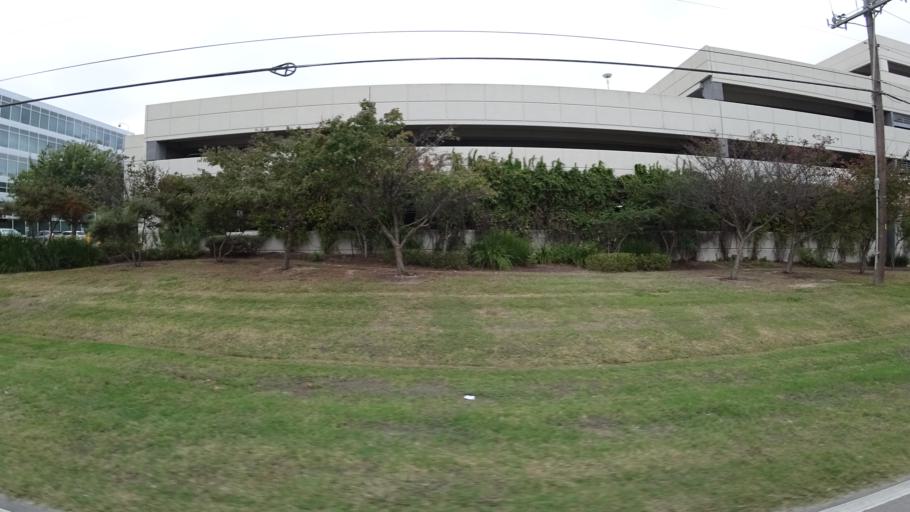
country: US
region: Texas
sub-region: Travis County
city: Wells Branch
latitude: 30.3996
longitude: -97.7190
